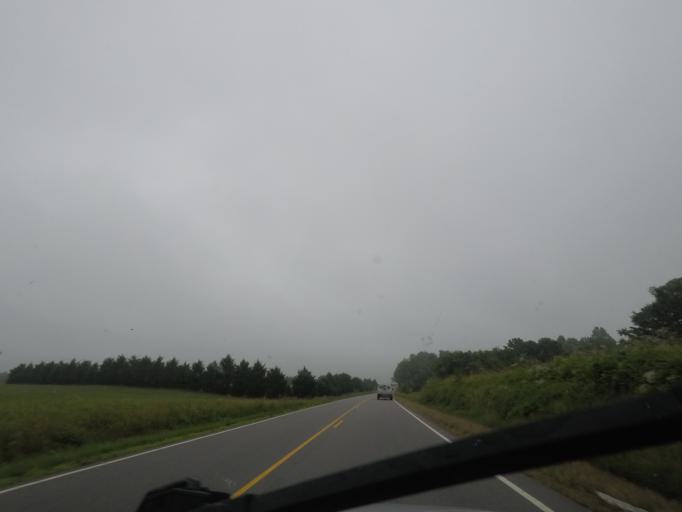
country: US
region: Virginia
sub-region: Prince Edward County
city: Farmville
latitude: 37.3554
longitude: -78.4812
